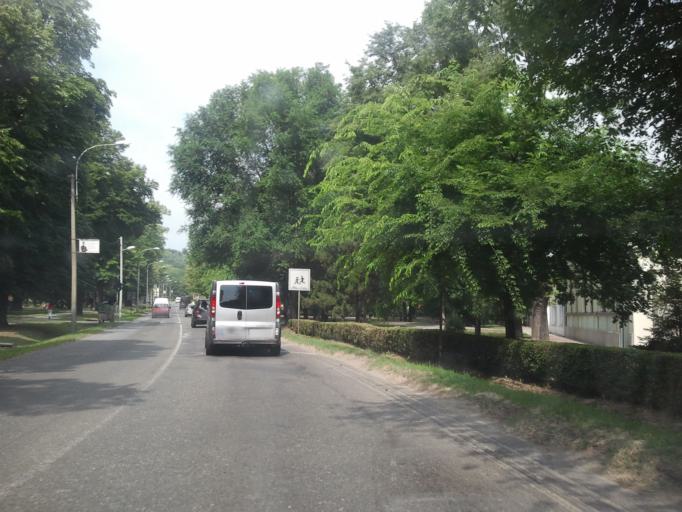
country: RS
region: Autonomna Pokrajina Vojvodina
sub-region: Juznobacki Okrug
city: Petrovaradin
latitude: 45.2523
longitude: 19.8715
